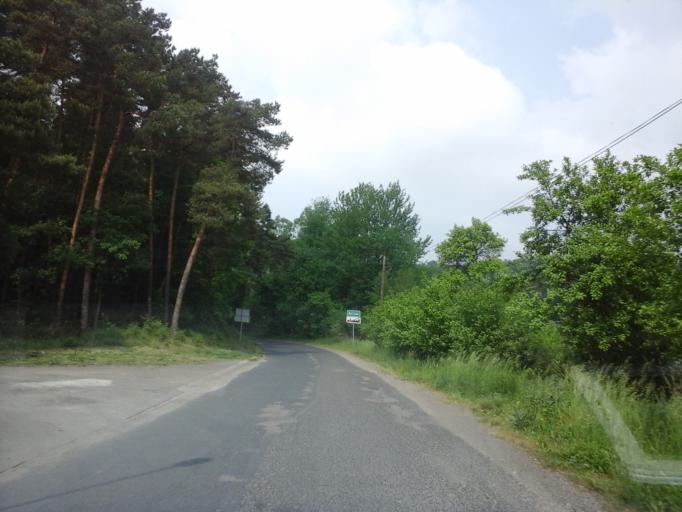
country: PL
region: West Pomeranian Voivodeship
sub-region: Powiat mysliborski
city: Barlinek
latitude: 53.0075
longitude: 15.2248
